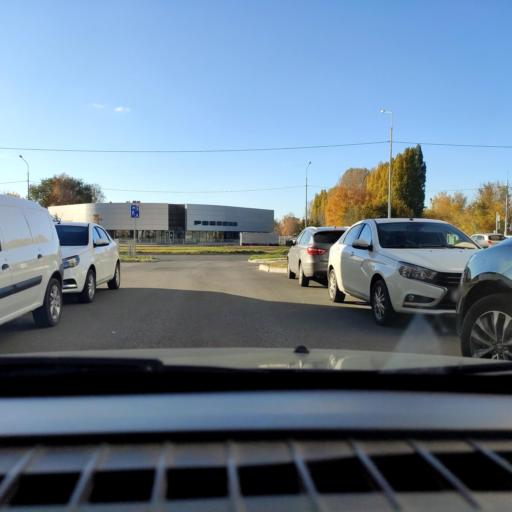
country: RU
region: Samara
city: Tol'yatti
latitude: 53.5020
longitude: 49.2705
